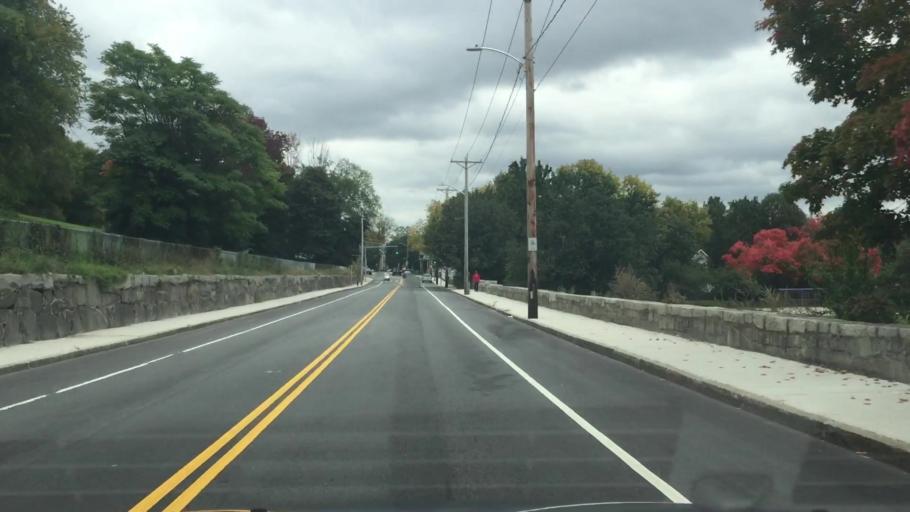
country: US
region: Massachusetts
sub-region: Middlesex County
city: Dracut
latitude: 42.6598
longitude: -71.3036
